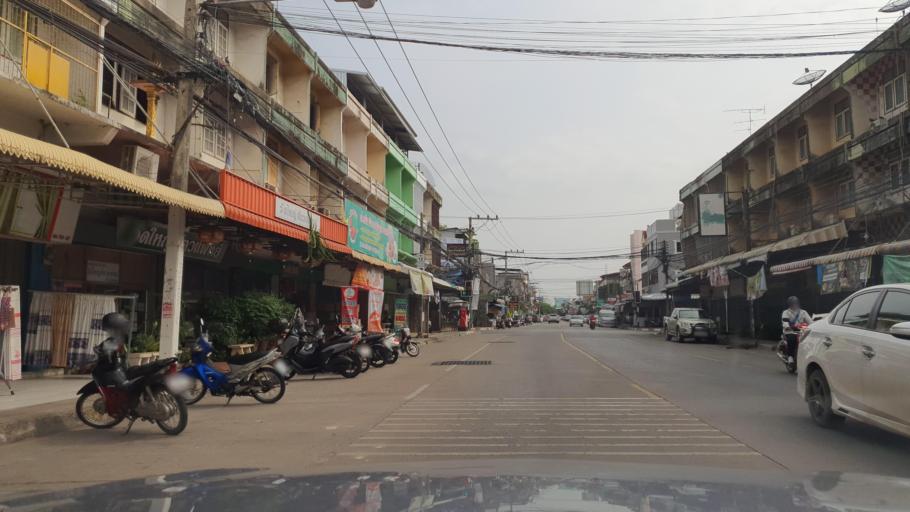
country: TH
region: Phitsanulok
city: Phitsanulok
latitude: 16.8250
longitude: 100.2650
